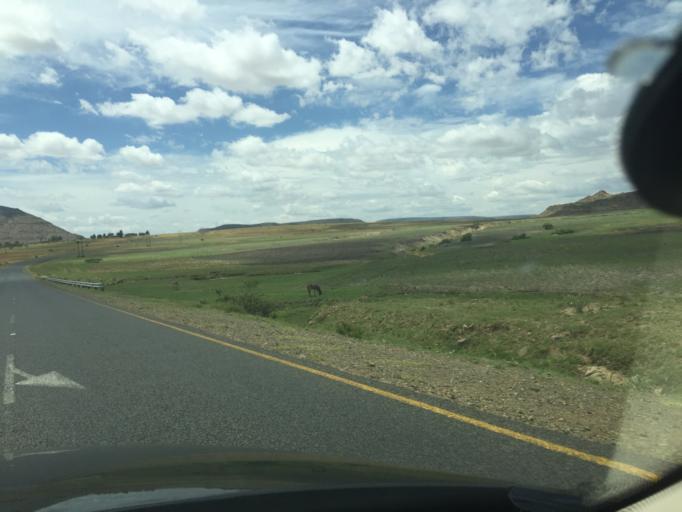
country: LS
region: Mafeteng
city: Mafeteng
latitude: -29.9216
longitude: 27.2528
